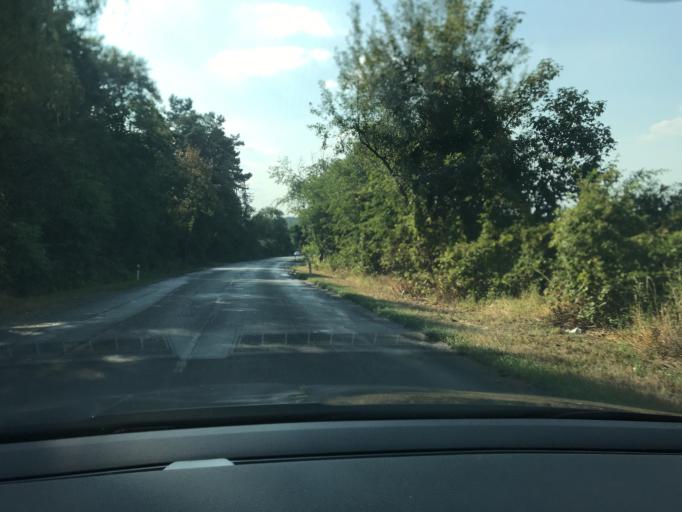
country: CZ
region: Central Bohemia
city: Kralupy nad Vltavou
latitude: 50.2172
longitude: 14.3071
